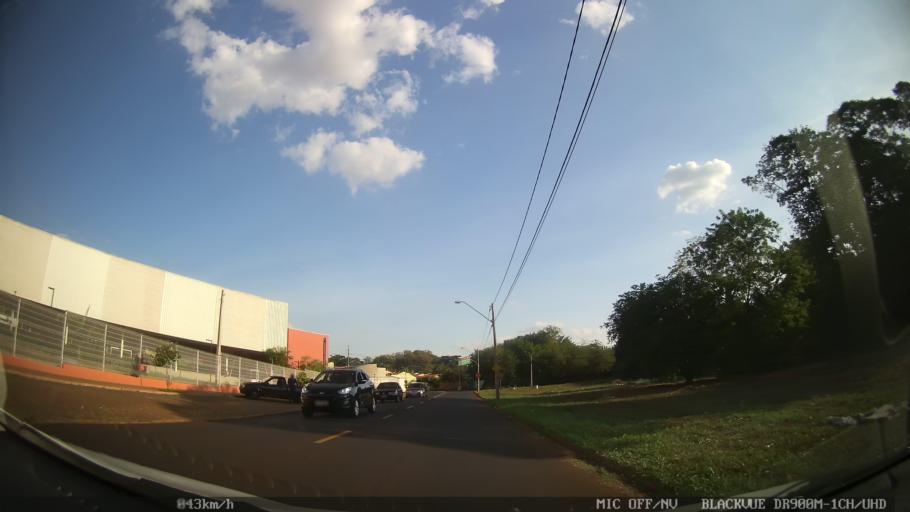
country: BR
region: Sao Paulo
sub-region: Ribeirao Preto
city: Ribeirao Preto
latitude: -21.1473
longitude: -47.8364
